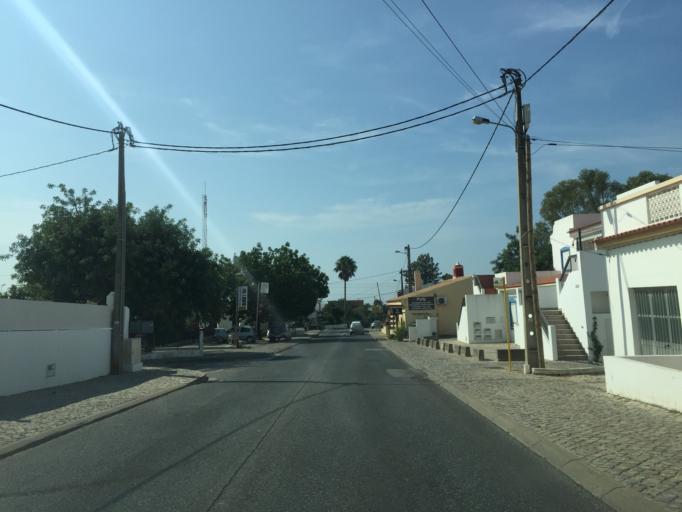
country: PT
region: Faro
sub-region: Loule
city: Almancil
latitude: 37.0957
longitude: -8.0246
